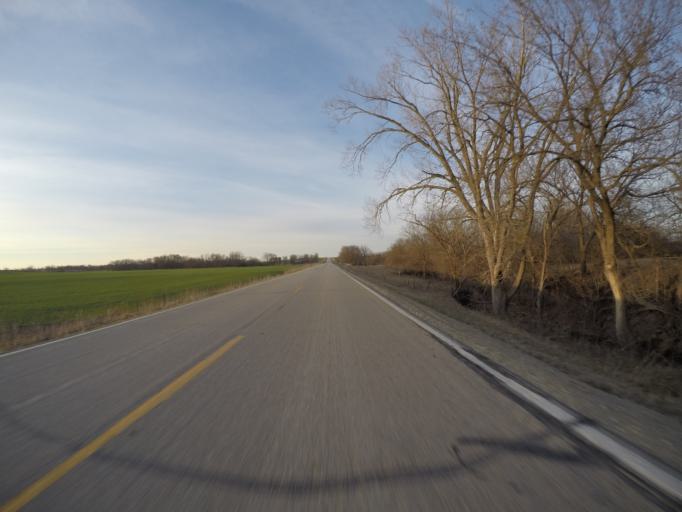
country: US
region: Kansas
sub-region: Riley County
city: Fort Riley North
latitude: 39.3815
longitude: -96.8494
